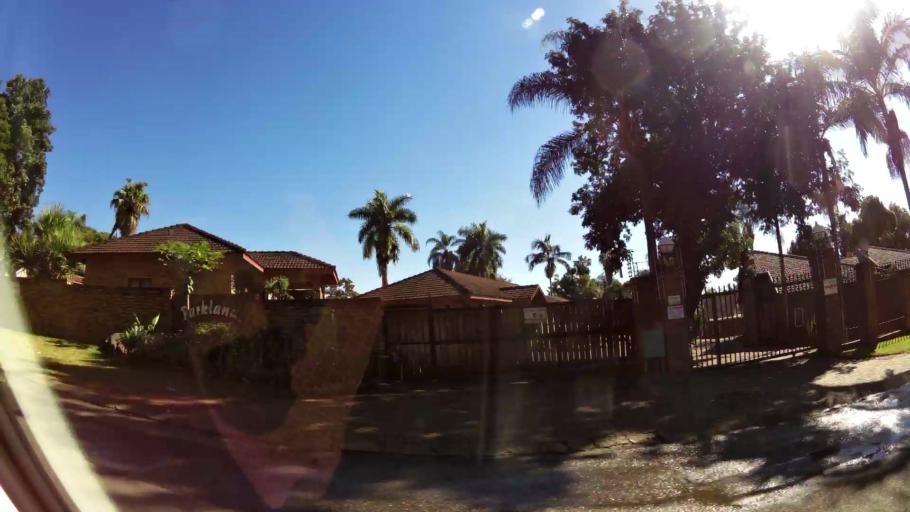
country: ZA
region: Limpopo
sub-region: Mopani District Municipality
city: Tzaneen
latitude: -23.8357
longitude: 30.1610
